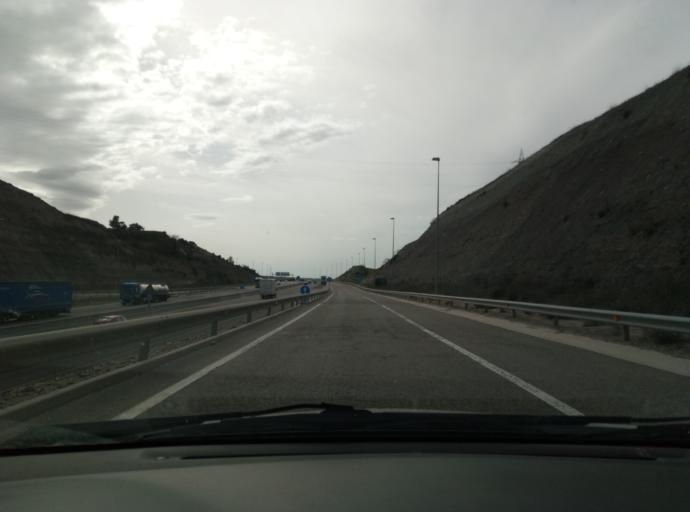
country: ES
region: Catalonia
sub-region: Provincia de Lleida
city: Sant Guim de Freixenet
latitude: 41.6226
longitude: 1.4060
